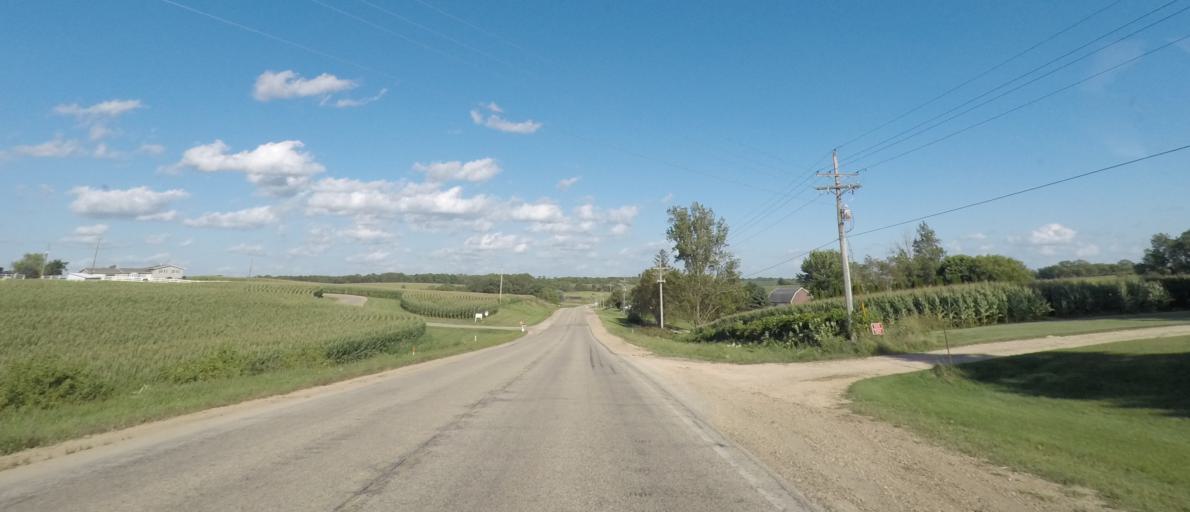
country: US
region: Wisconsin
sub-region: Iowa County
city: Dodgeville
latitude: 42.9816
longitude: -90.0852
